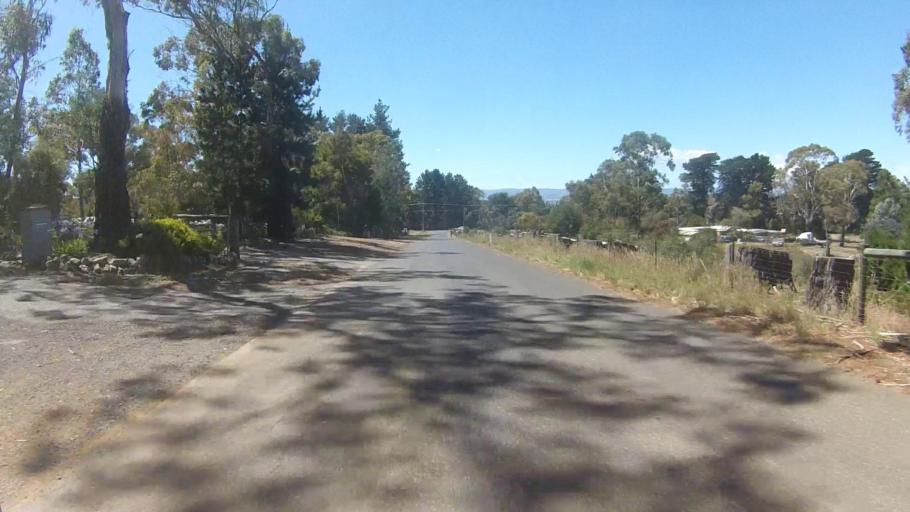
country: AU
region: Tasmania
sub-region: Clarence
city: Cambridge
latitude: -42.8397
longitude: 147.4629
